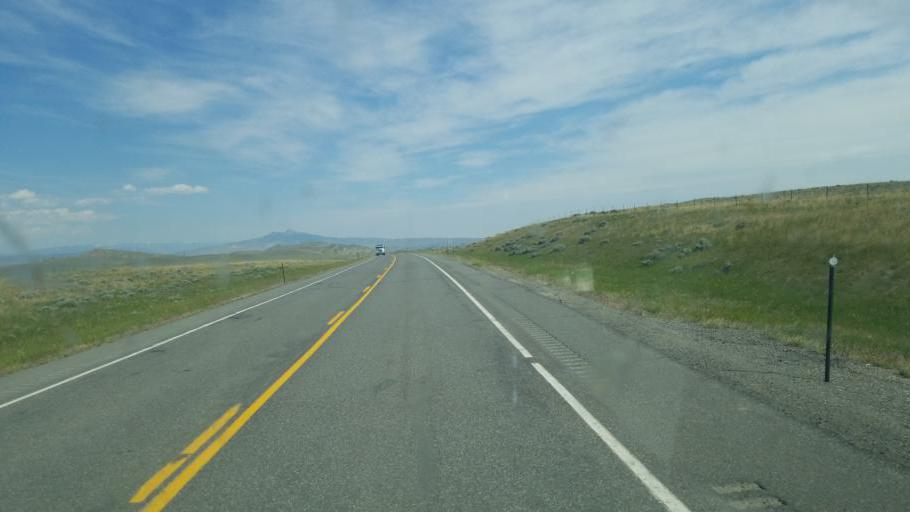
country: US
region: Wyoming
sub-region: Park County
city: Cody
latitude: 44.4303
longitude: -109.0114
